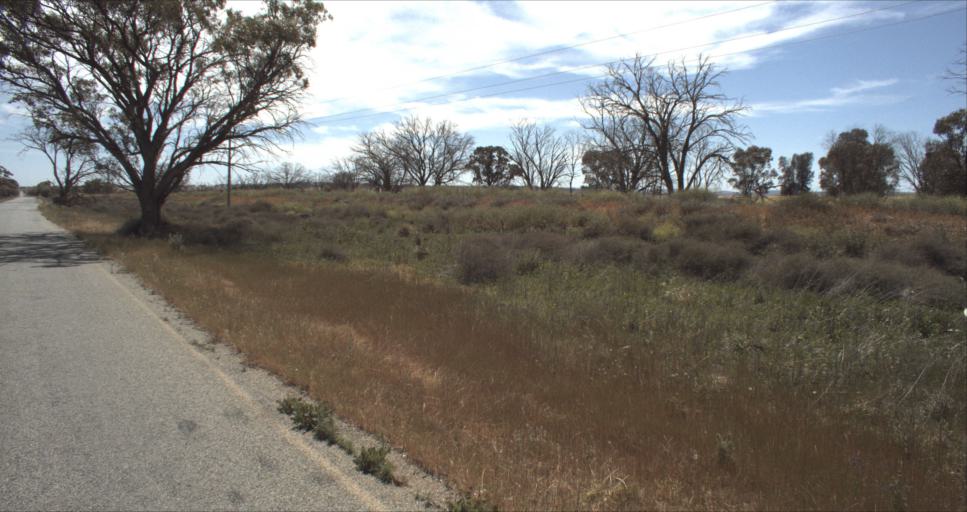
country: AU
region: New South Wales
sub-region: Leeton
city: Leeton
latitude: -34.6417
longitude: 146.4672
